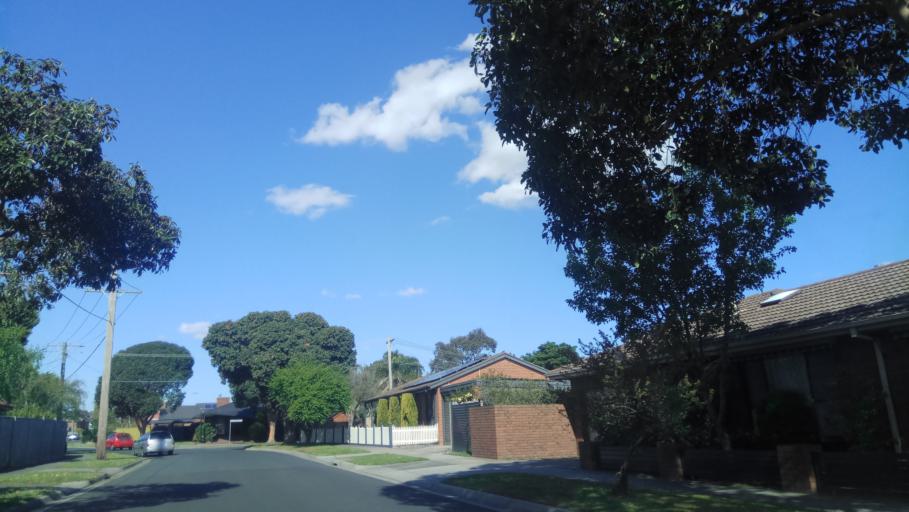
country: AU
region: Victoria
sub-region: Kingston
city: Dingley Village
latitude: -37.9881
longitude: 145.1319
